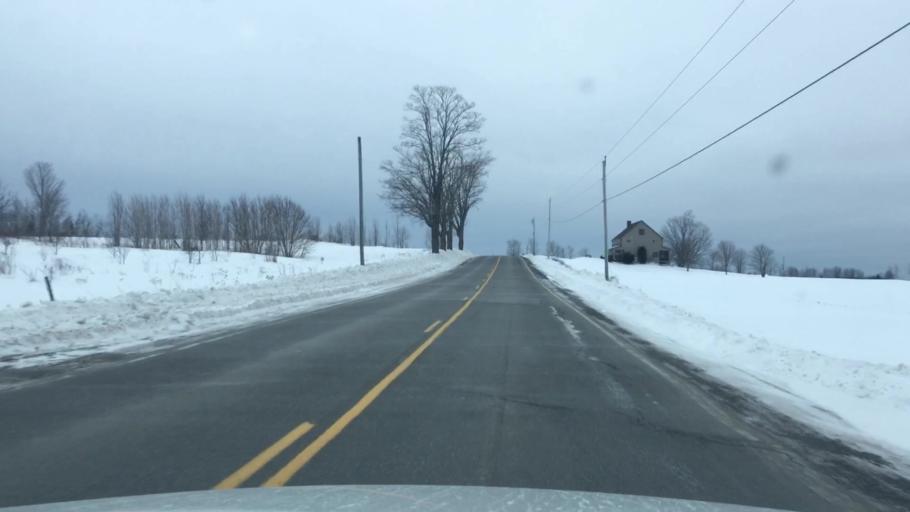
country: US
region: Maine
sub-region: Penobscot County
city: Corinna
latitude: 44.9459
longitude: -69.2102
